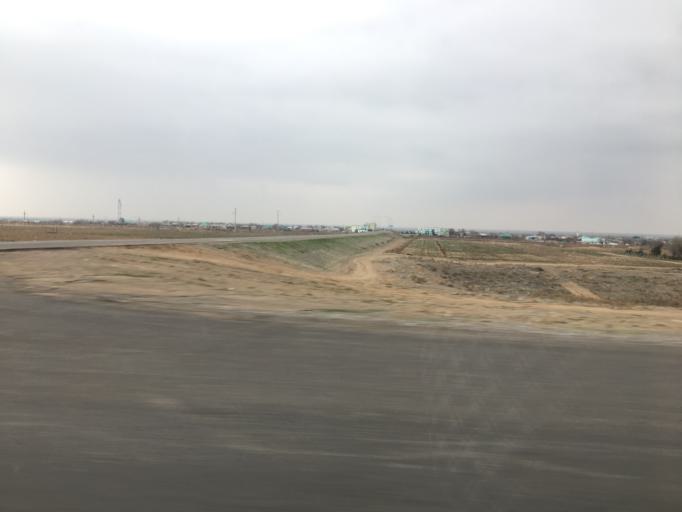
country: IR
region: Razavi Khorasan
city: Dargaz
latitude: 37.6425
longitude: 59.1416
